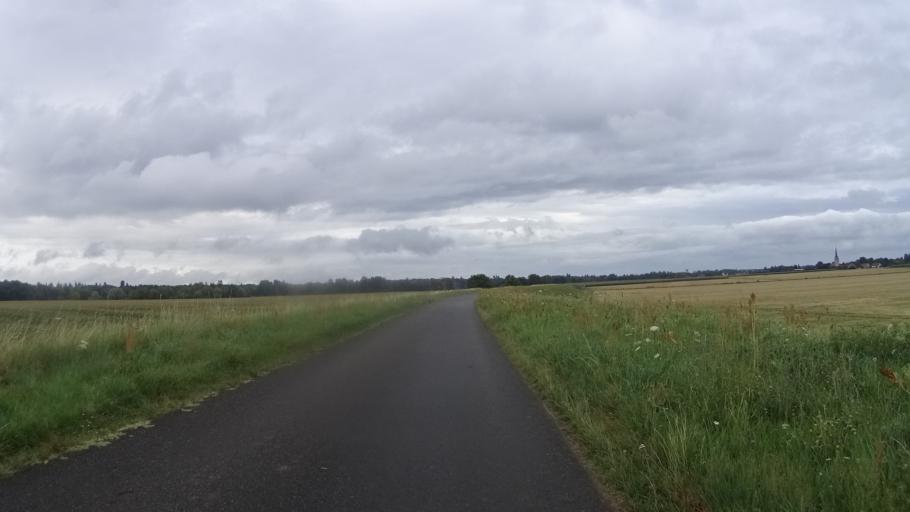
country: FR
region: Centre
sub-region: Departement du Loiret
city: Darvoy
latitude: 47.8639
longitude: 2.0806
